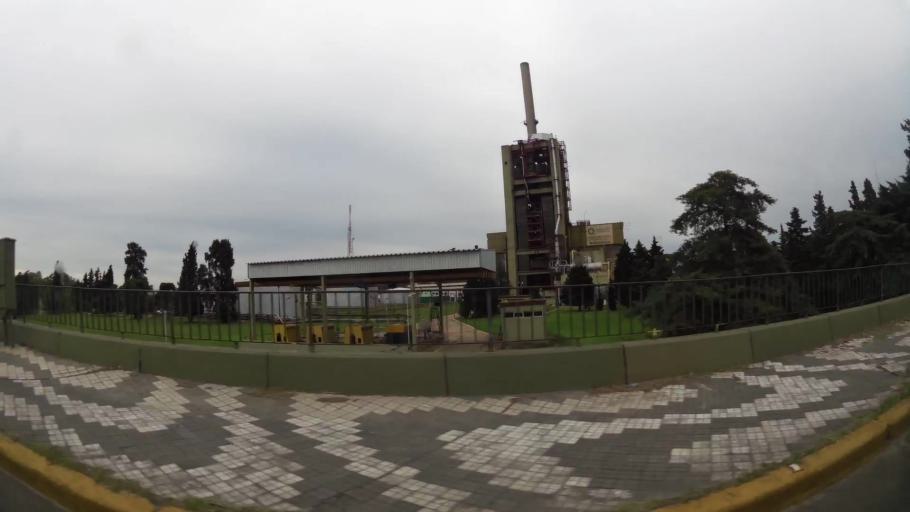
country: AR
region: Santa Fe
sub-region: Departamento de Rosario
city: Rosario
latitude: -32.9045
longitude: -60.6786
